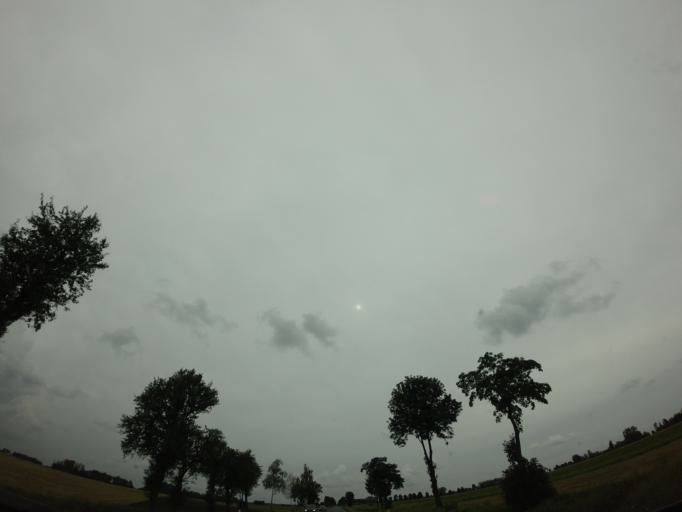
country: PL
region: Masovian Voivodeship
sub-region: Powiat ciechanowski
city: Golymin-Osrodek
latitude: 52.8301
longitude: 20.9229
